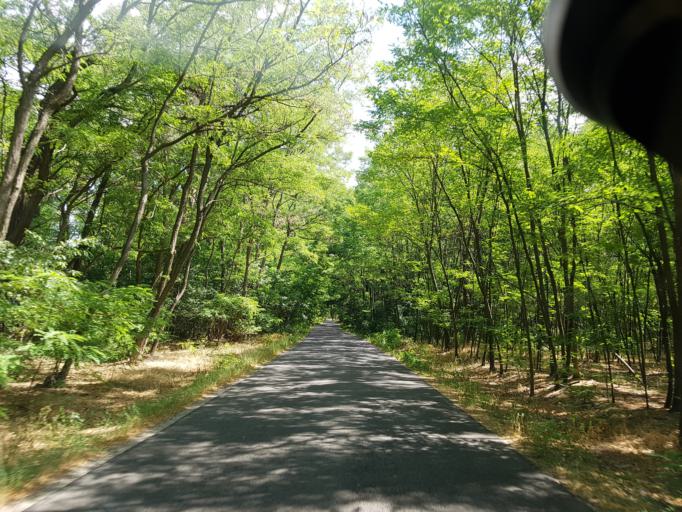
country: DE
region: Brandenburg
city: Drebkau
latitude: 51.6763
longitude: 14.3032
